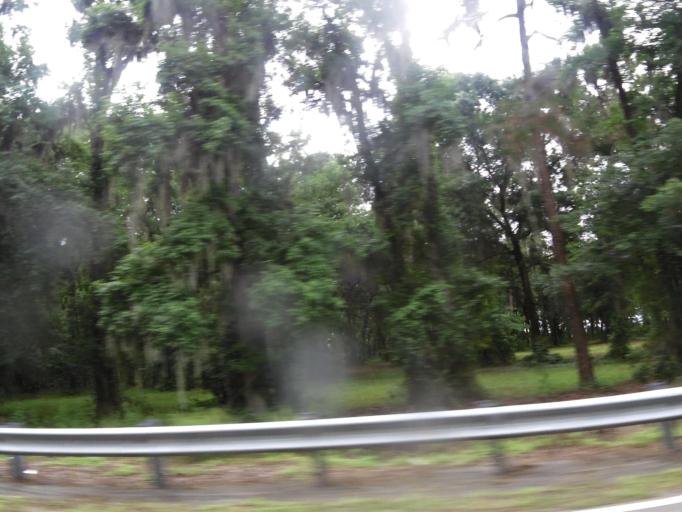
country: US
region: Florida
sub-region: Saint Johns County
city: Saint Augustine South
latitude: 29.8513
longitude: -81.5147
